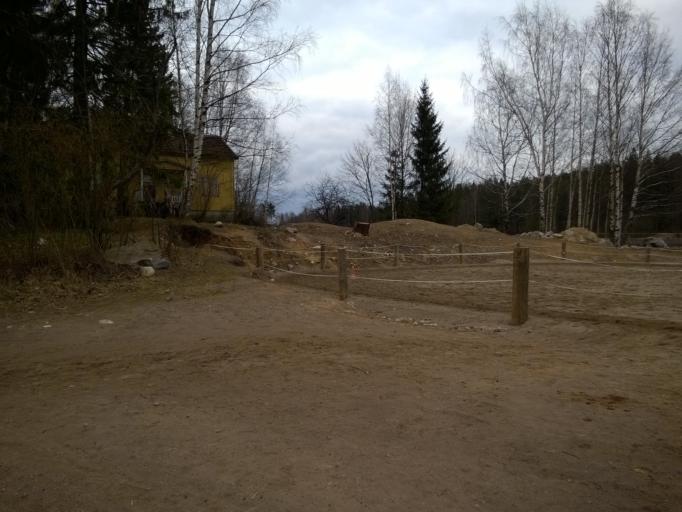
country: FI
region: Uusimaa
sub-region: Helsinki
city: Vantaa
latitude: 60.2274
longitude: 25.0410
